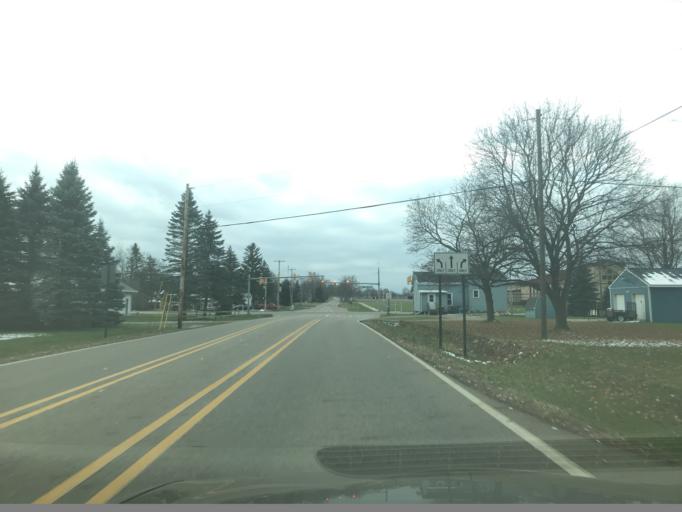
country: US
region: Michigan
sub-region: Eaton County
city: Waverly
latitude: 42.7277
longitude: -84.6817
